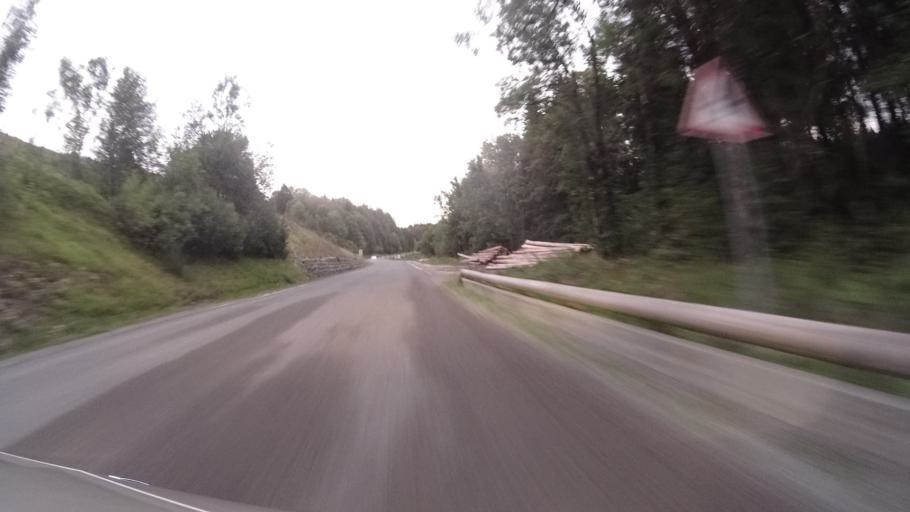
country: FR
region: Franche-Comte
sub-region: Departement du Jura
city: Morbier
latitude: 46.6659
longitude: 6.0873
